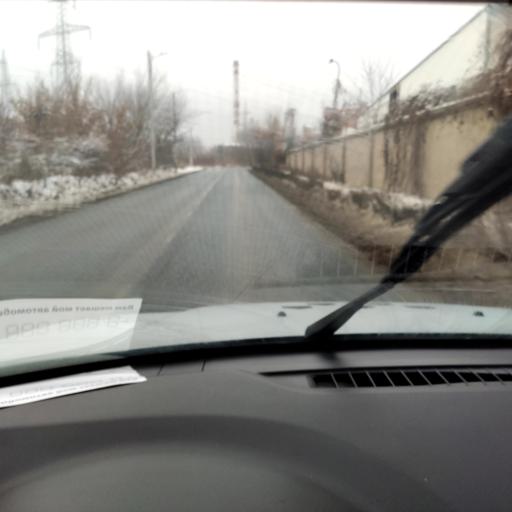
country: RU
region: Samara
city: Zhigulevsk
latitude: 53.5158
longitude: 49.4736
